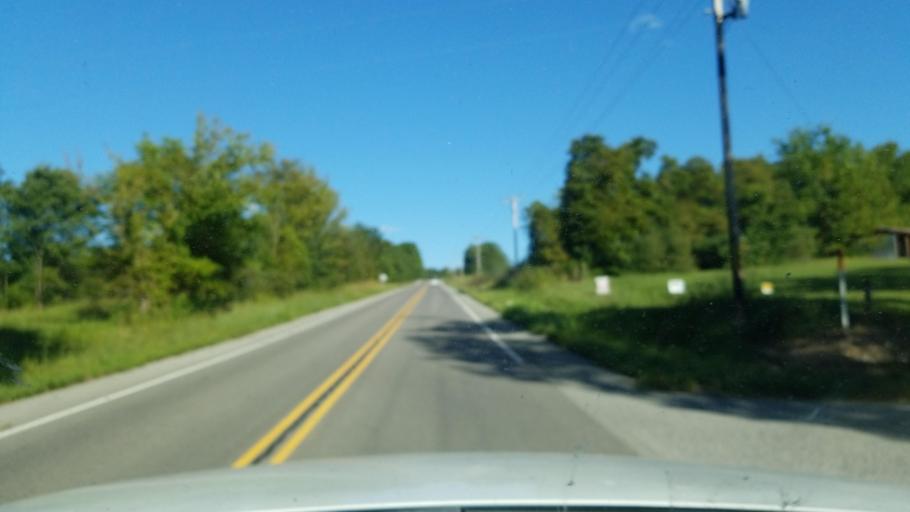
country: US
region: Illinois
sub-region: Hardin County
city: Rosiclare
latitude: 37.5753
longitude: -88.4270
